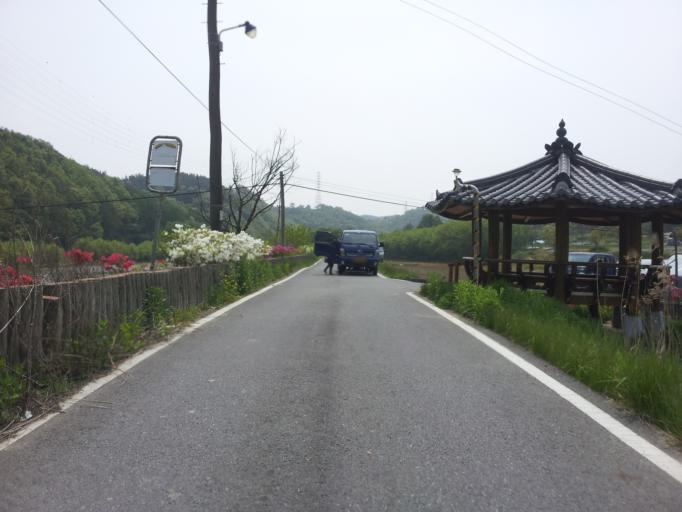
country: KR
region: Daejeon
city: Daejeon
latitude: 36.2630
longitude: 127.2959
